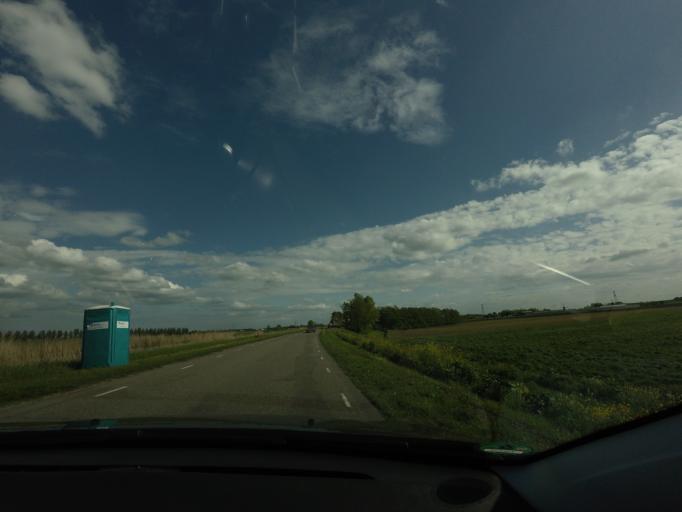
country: NL
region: North Holland
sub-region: Gemeente Heerhugowaard
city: Heerhugowaard
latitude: 52.6460
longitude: 4.8700
